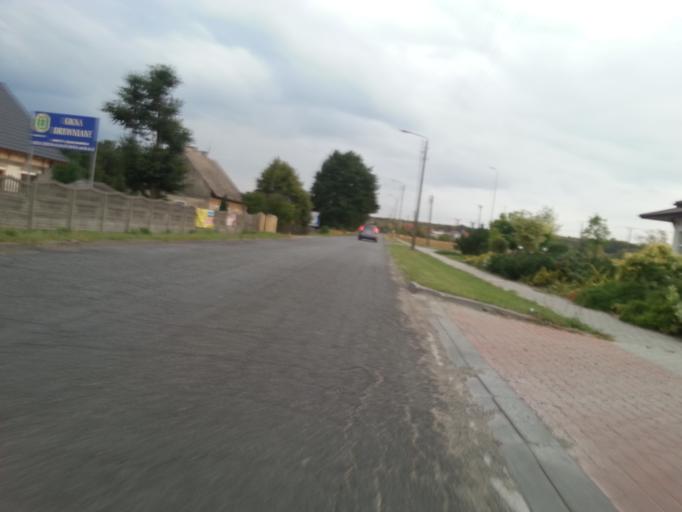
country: PL
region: Lower Silesian Voivodeship
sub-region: Powiat olesnicki
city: Twardogora
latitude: 51.3588
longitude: 17.4558
